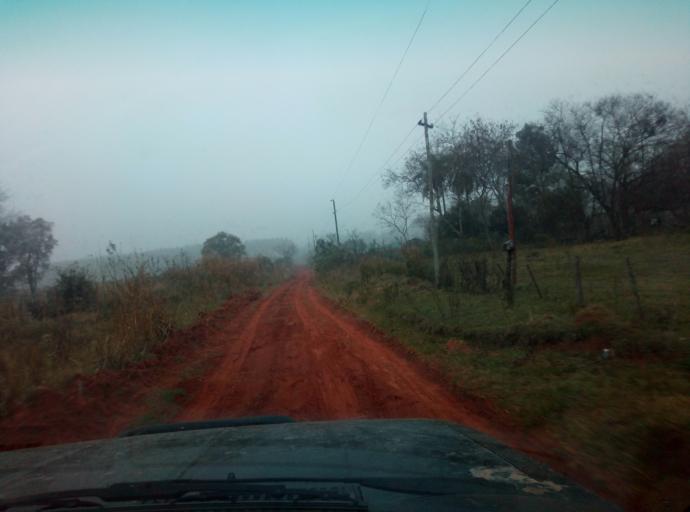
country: PY
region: Caaguazu
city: Doctor Cecilio Baez
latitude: -25.1596
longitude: -56.2617
